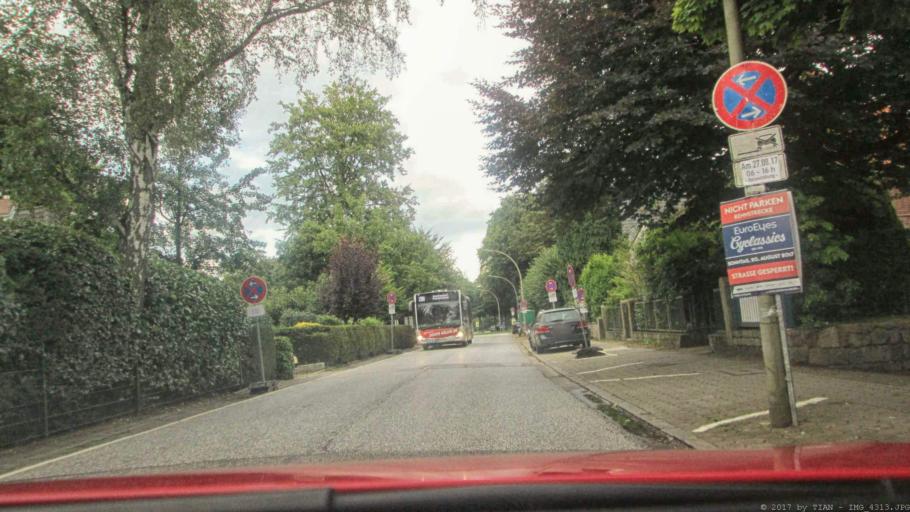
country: DE
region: Schleswig-Holstein
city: Rellingen
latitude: 53.5663
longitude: 9.7951
